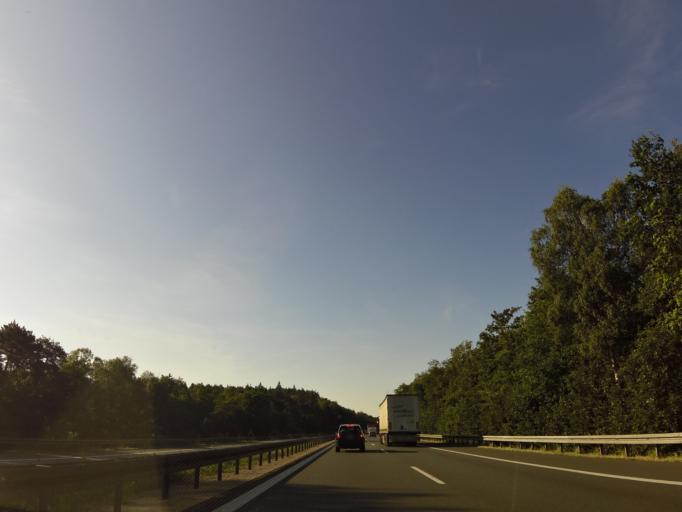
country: DE
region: Bavaria
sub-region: Regierungsbezirk Mittelfranken
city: Hessdorf
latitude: 49.6151
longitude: 10.9242
